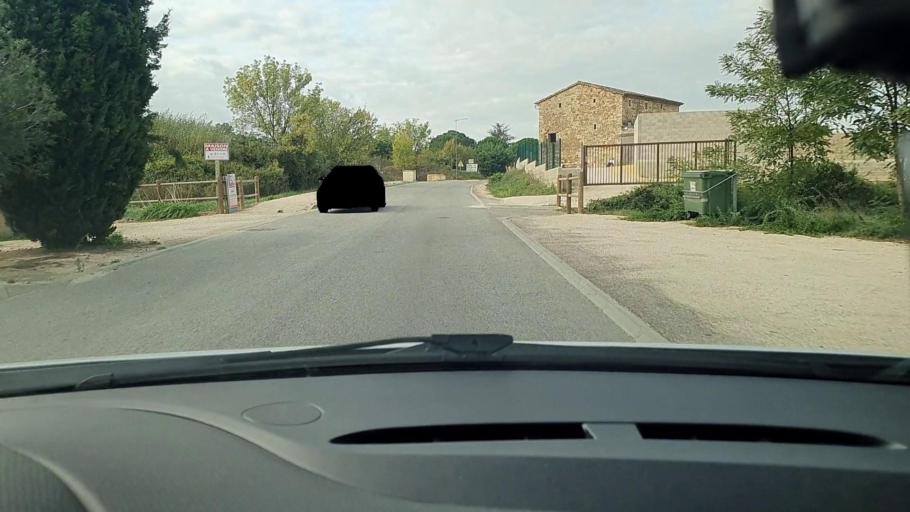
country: FR
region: Languedoc-Roussillon
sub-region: Departement du Gard
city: Saint-Ambroix
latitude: 44.2242
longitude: 4.2704
